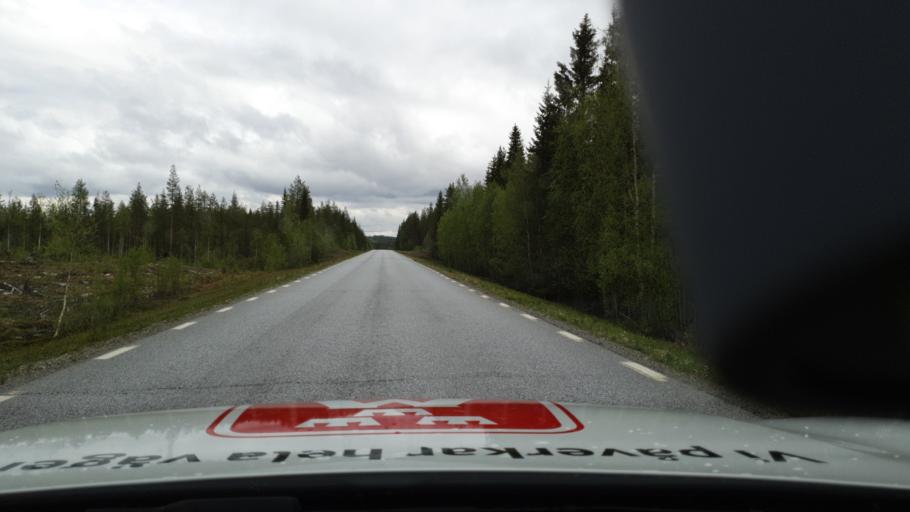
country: SE
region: Vaesterbotten
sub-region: Vilhelmina Kommun
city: Sjoberg
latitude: 64.8081
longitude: 15.9818
